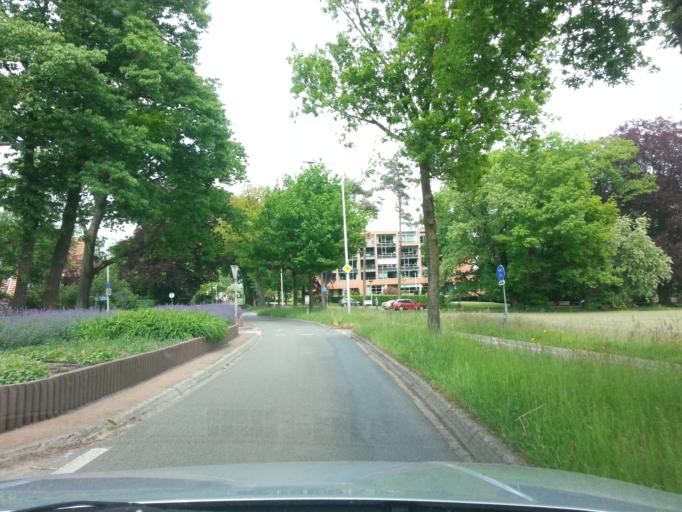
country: NL
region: Gelderland
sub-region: Gemeente Lochem
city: Lochem
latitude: 52.1484
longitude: 6.4198
